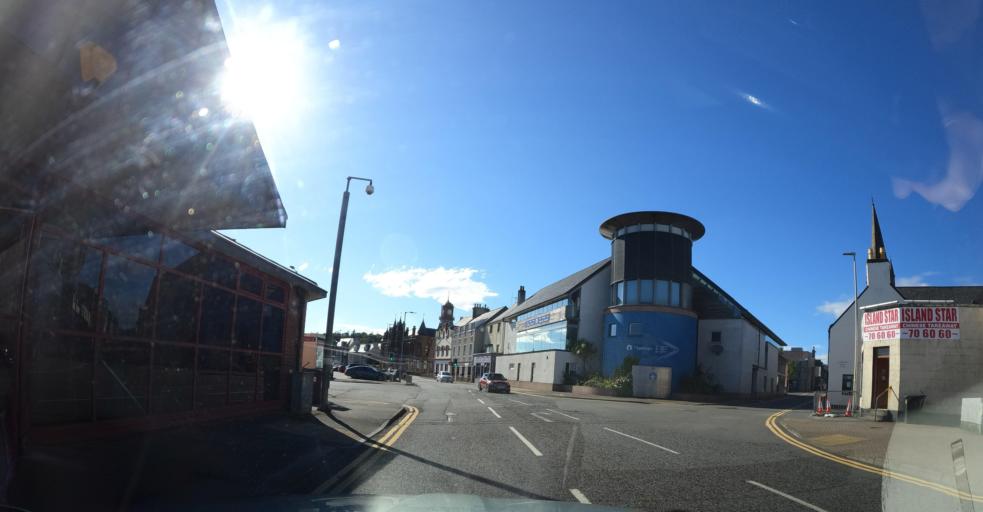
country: GB
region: Scotland
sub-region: Eilean Siar
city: Stornoway
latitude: 58.2078
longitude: -6.3865
